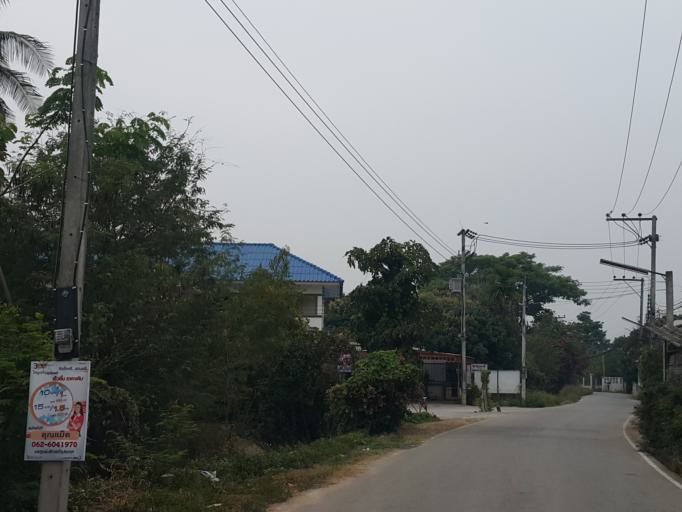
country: TH
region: Chiang Mai
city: Saraphi
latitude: 18.7228
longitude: 99.0045
